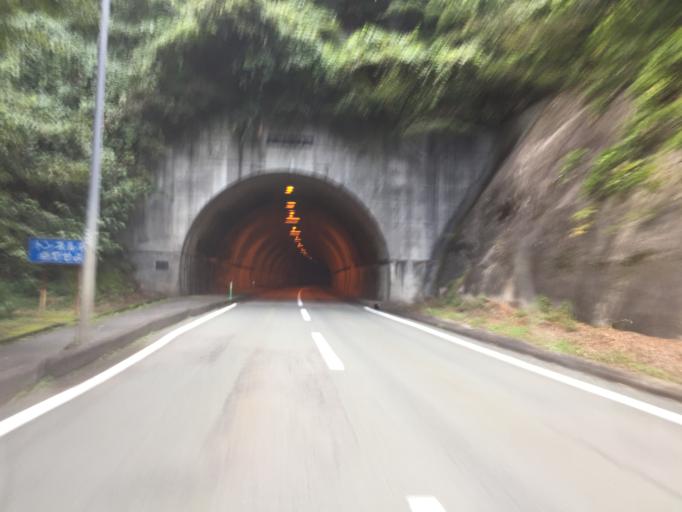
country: JP
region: Fukushima
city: Namie
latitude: 37.5260
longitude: 140.8799
